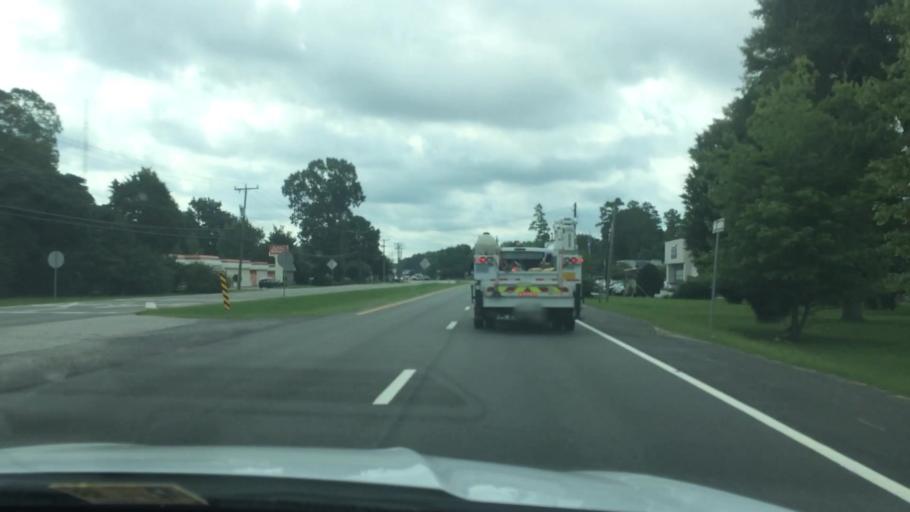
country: US
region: Virginia
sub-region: York County
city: Yorktown
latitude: 37.1836
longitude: -76.4839
